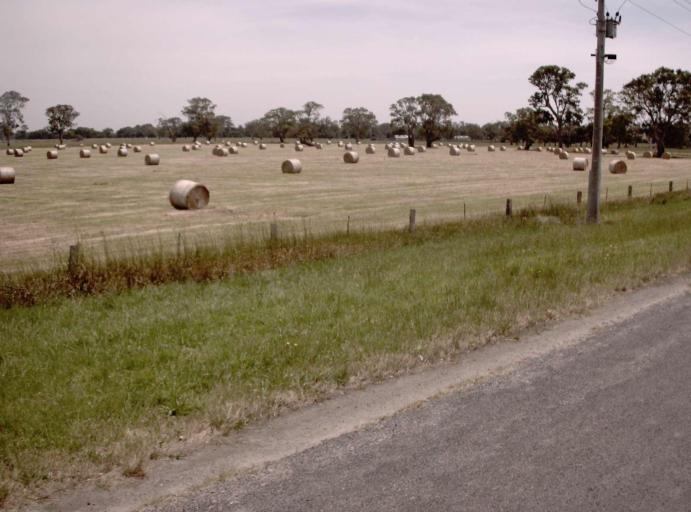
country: AU
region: Victoria
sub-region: Frankston
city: Skye
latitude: -38.0848
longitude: 145.2379
